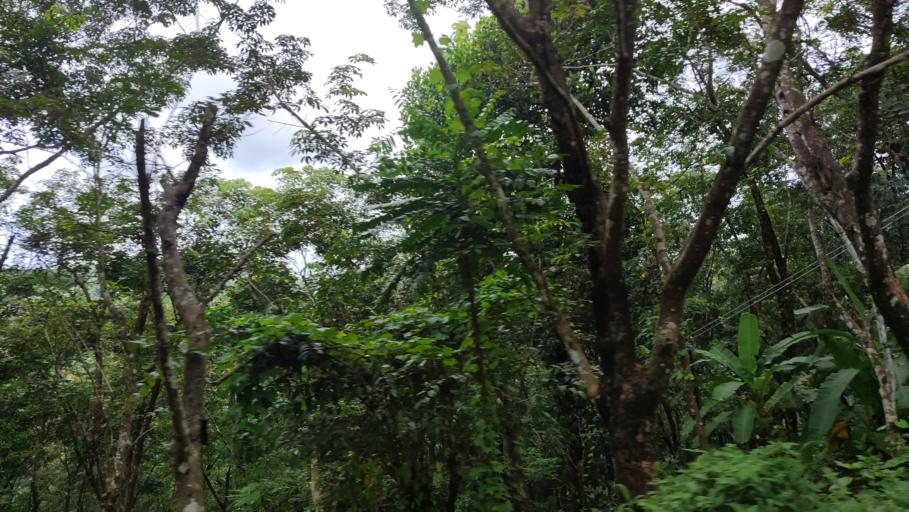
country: IN
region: Kerala
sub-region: Kasaragod District
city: Nileshwar
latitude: 12.2975
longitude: 75.2908
